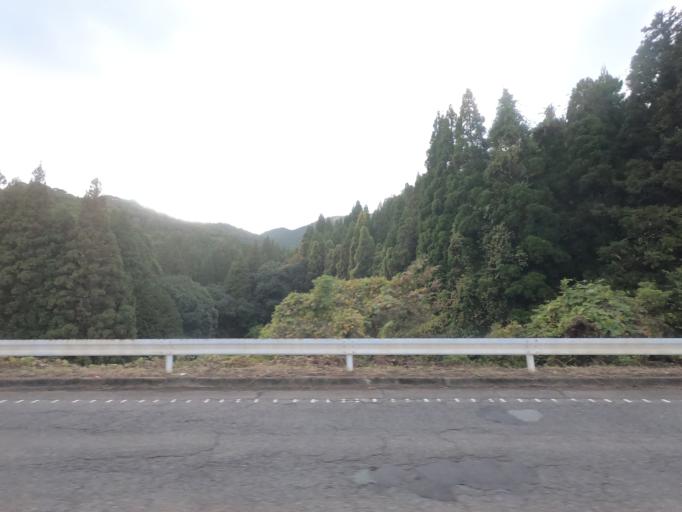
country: JP
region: Kumamoto
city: Minamata
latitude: 32.2511
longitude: 130.5028
